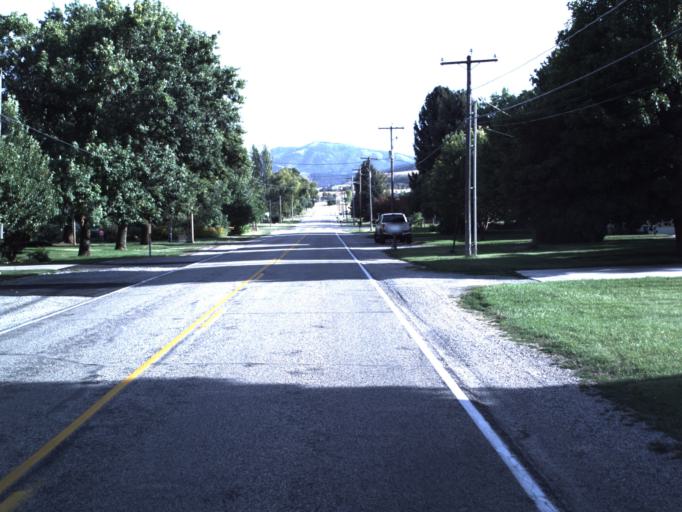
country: US
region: Utah
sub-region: Cache County
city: Wellsville
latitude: 41.6257
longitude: -111.9349
